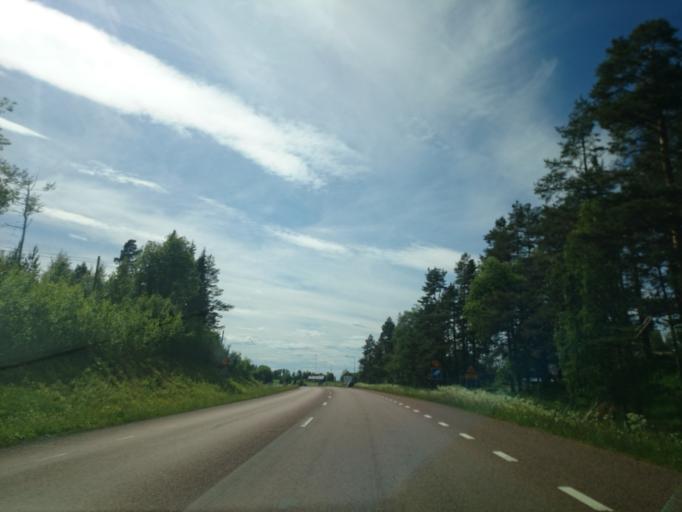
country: SE
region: Jaemtland
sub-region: Krokoms Kommun
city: Krokom
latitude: 63.3255
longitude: 14.3080
